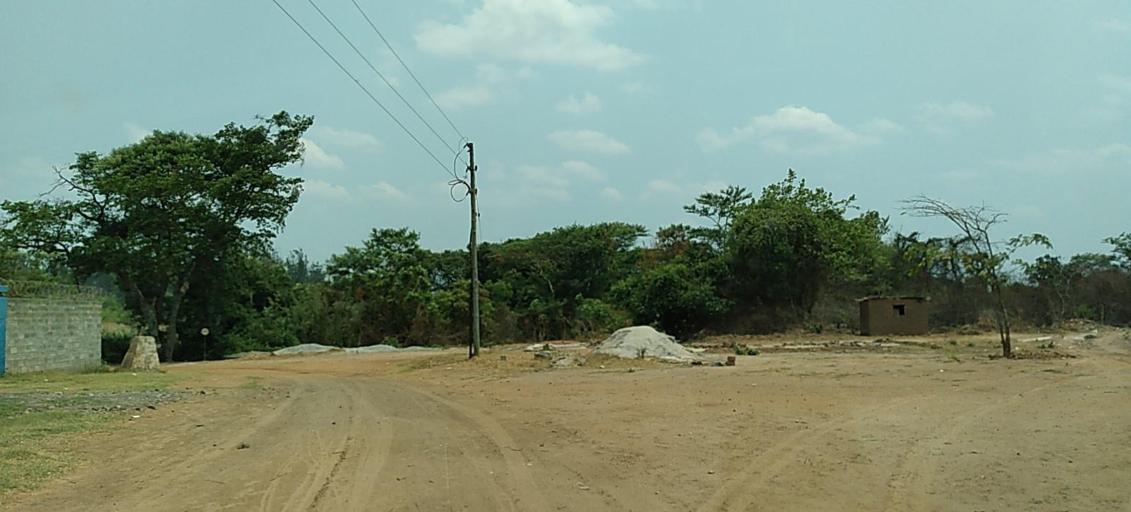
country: ZM
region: Copperbelt
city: Kalulushi
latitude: -12.7600
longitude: 28.0308
